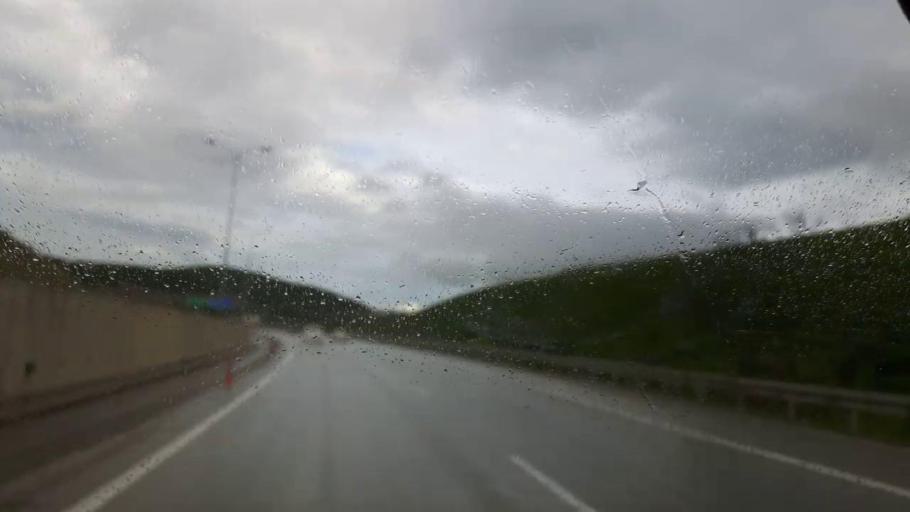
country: GE
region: Shida Kartli
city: Kaspi
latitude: 41.9960
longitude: 44.4094
